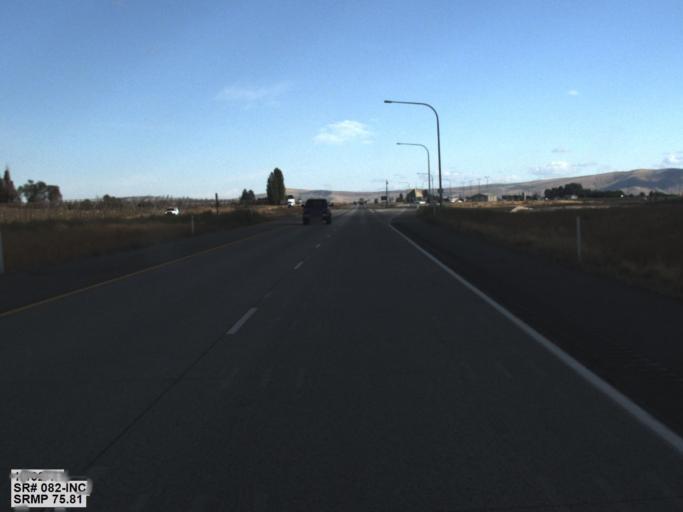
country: US
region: Washington
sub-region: Yakima County
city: Grandview
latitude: 46.2503
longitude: -119.8651
